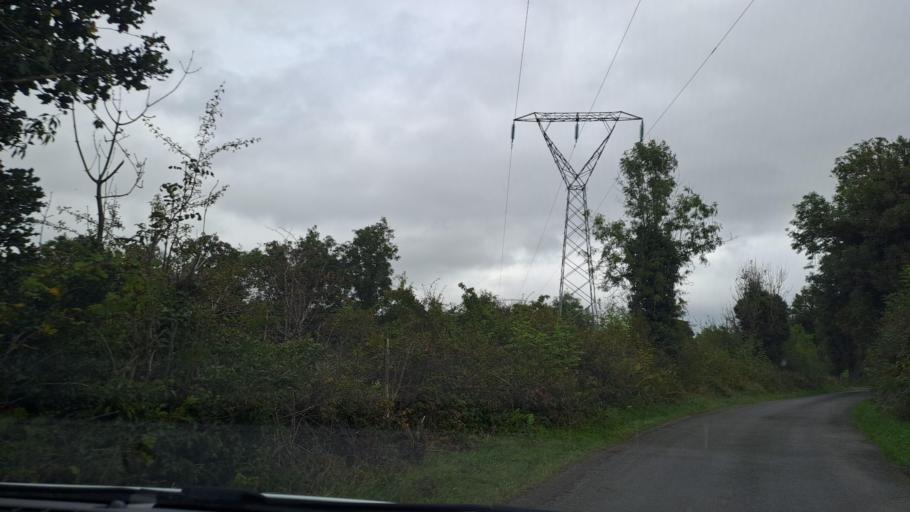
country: IE
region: Ulster
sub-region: An Cabhan
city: Bailieborough
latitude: 54.0133
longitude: -6.9404
